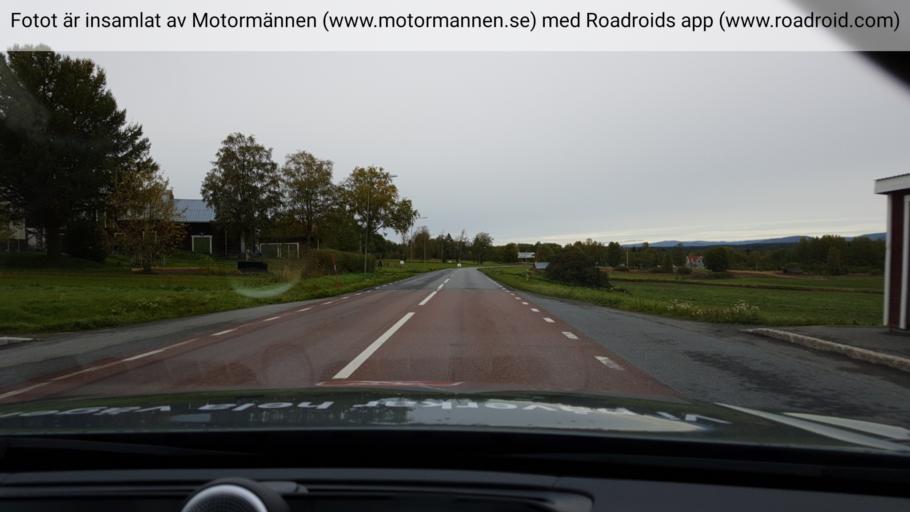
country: SE
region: Jaemtland
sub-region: Stroemsunds Kommun
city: Stroemsund
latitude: 63.8197
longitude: 15.5166
